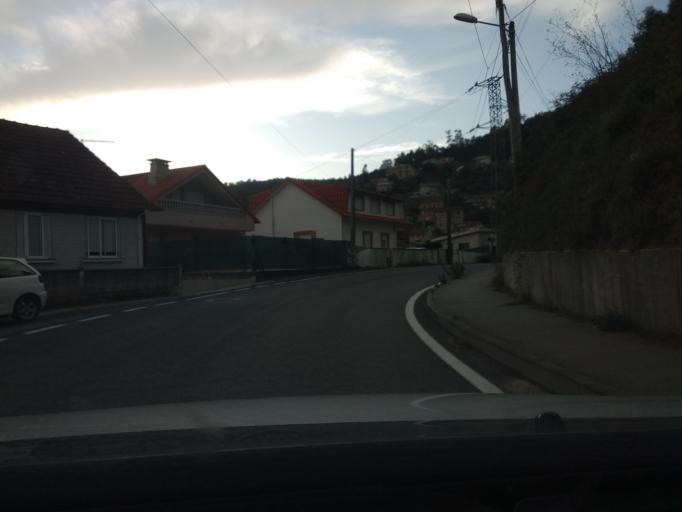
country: ES
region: Galicia
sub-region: Provincia de Pontevedra
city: Redondela
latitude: 42.2936
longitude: -8.6790
